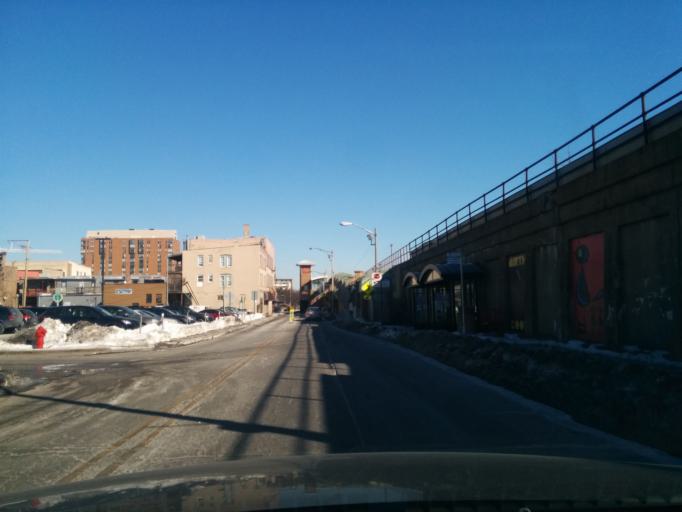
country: US
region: Illinois
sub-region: Cook County
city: Forest Park
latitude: 41.8872
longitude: -87.8041
